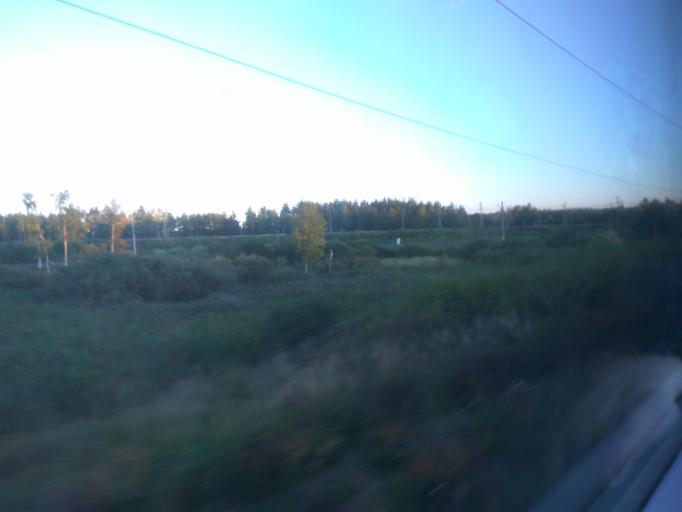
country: RU
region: Moskovskaya
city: Fryazevo
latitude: 55.7374
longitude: 38.4773
